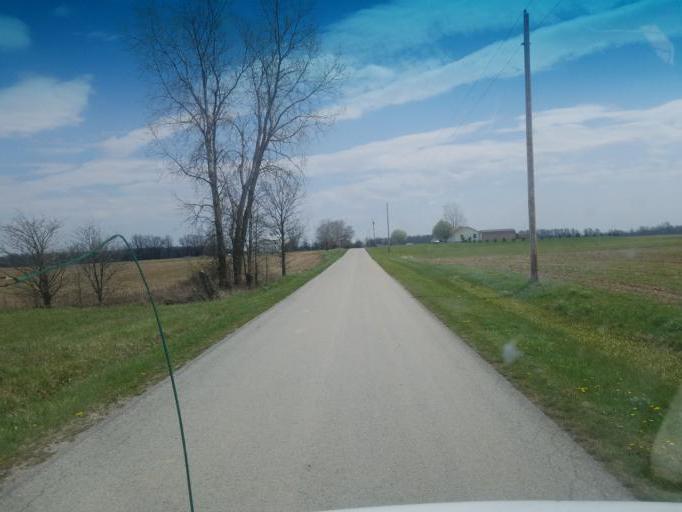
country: US
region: Ohio
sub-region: Hardin County
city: Forest
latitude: 40.7742
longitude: -83.4440
